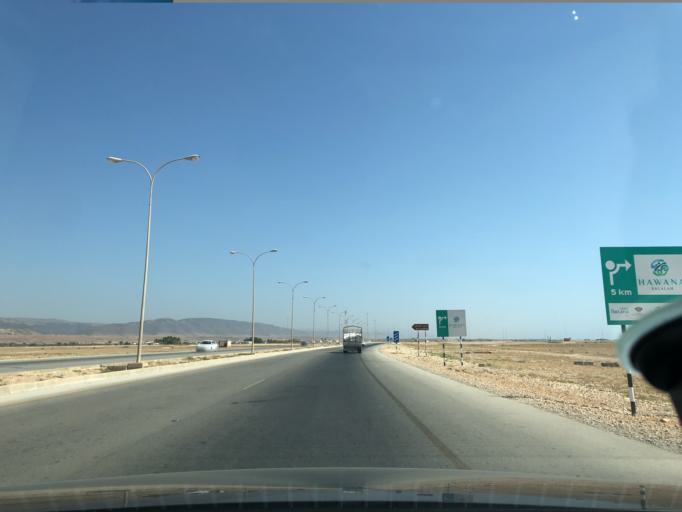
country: OM
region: Zufar
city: Salalah
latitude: 17.0532
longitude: 54.2706
